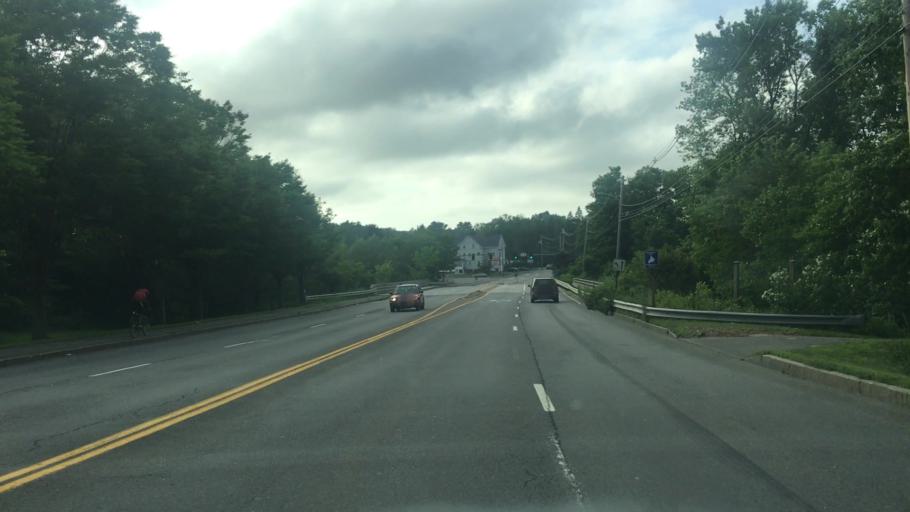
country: US
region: Maine
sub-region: Cumberland County
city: Westbrook
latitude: 43.7026
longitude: -70.3239
